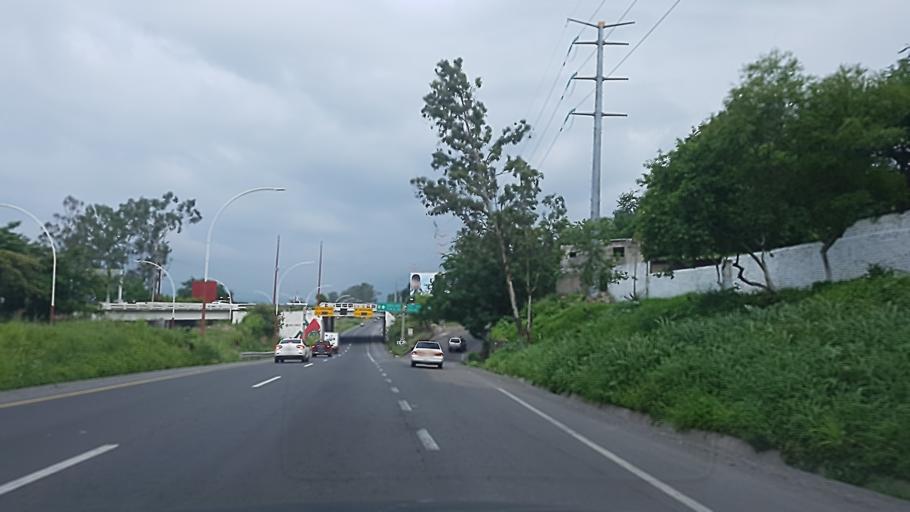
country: MX
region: Nayarit
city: Xalisco
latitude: 21.4720
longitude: -104.8903
